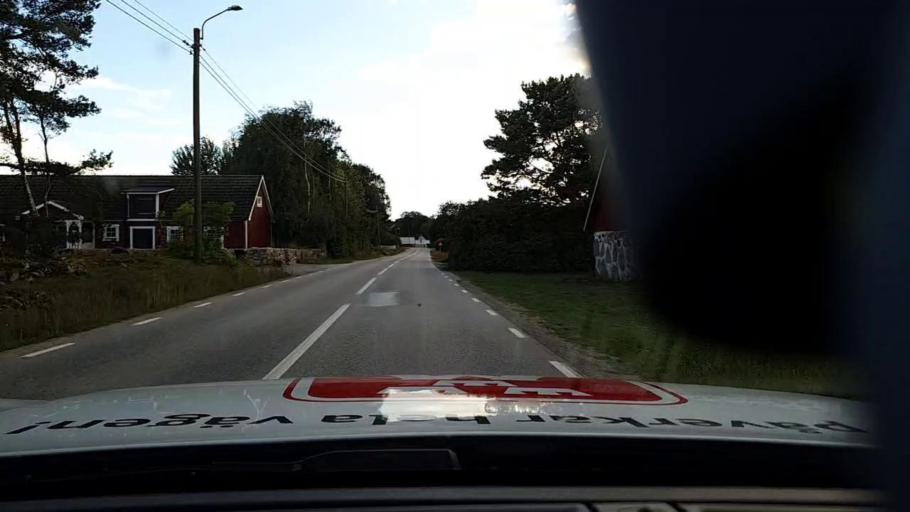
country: SE
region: Blekinge
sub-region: Solvesborgs Kommun
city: Soelvesborg
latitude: 56.0233
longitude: 14.7180
